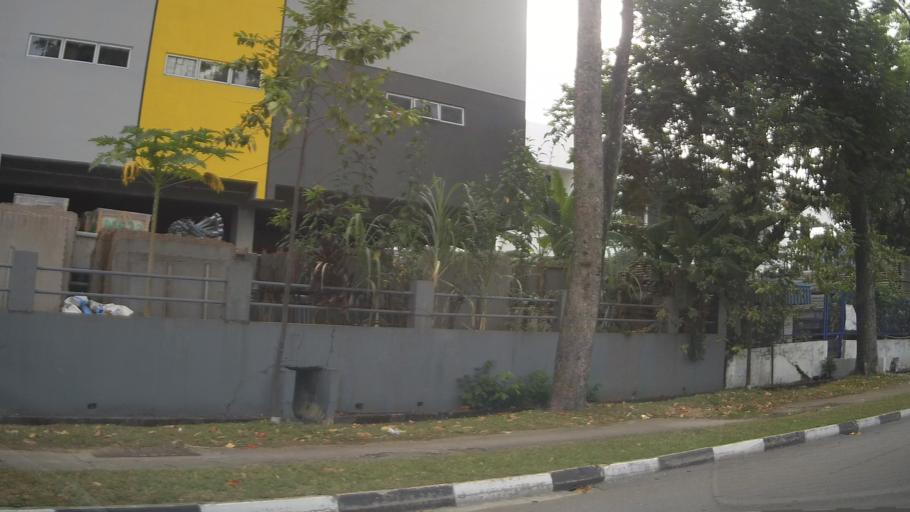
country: MY
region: Johor
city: Johor Bahru
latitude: 1.3203
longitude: 103.6469
